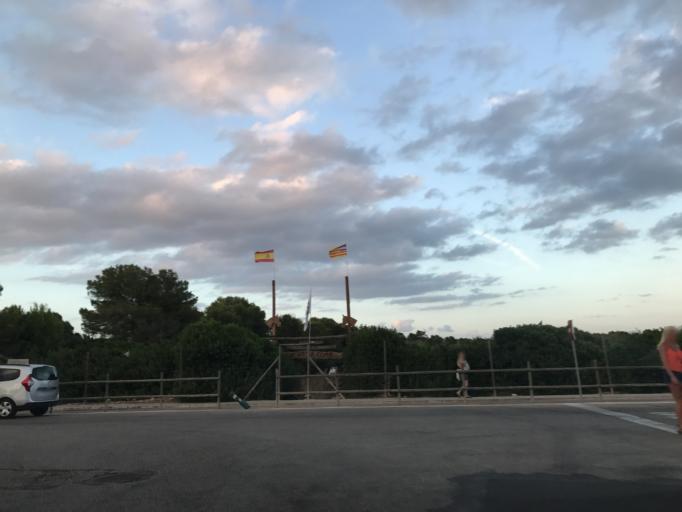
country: ES
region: Balearic Islands
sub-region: Illes Balears
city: Son Servera
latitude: 39.5767
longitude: 3.3774
